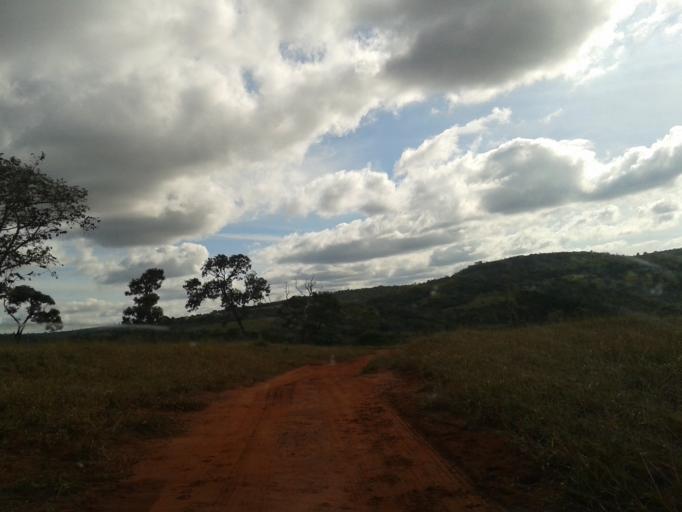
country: BR
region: Minas Gerais
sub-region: Campina Verde
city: Campina Verde
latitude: -19.4423
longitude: -49.7320
